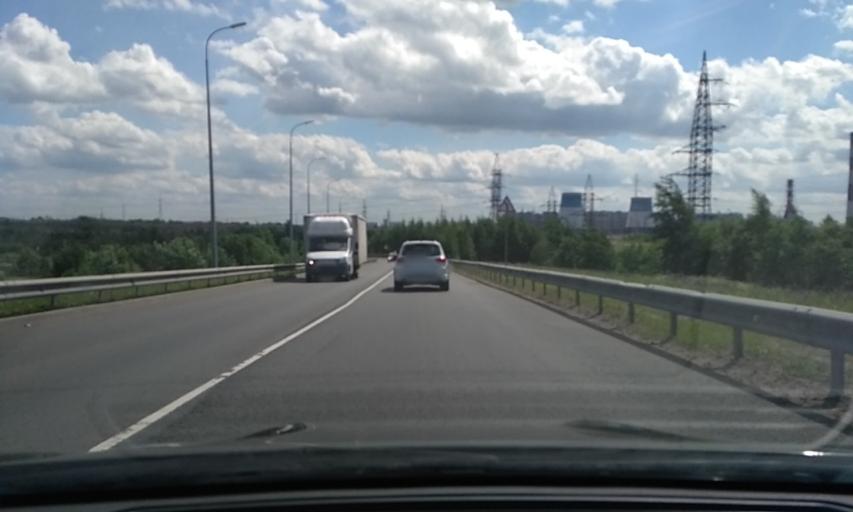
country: RU
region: Leningrad
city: Rybatskoye
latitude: 59.8869
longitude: 30.5059
